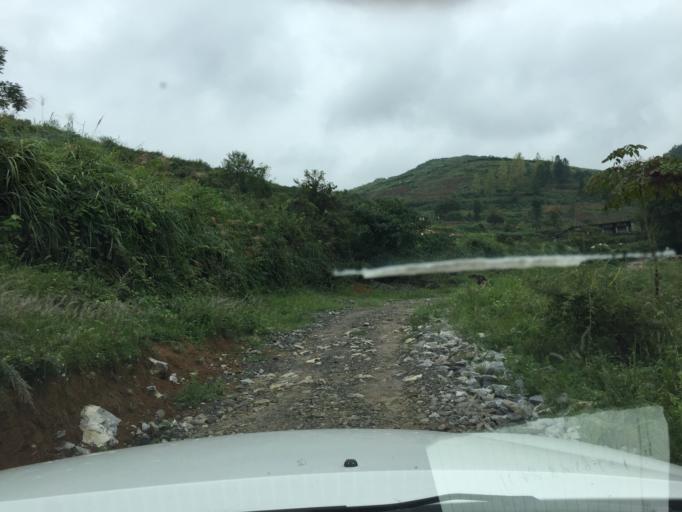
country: CN
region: Guizhou Sheng
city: Yantang
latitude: 28.2010
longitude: 108.0821
